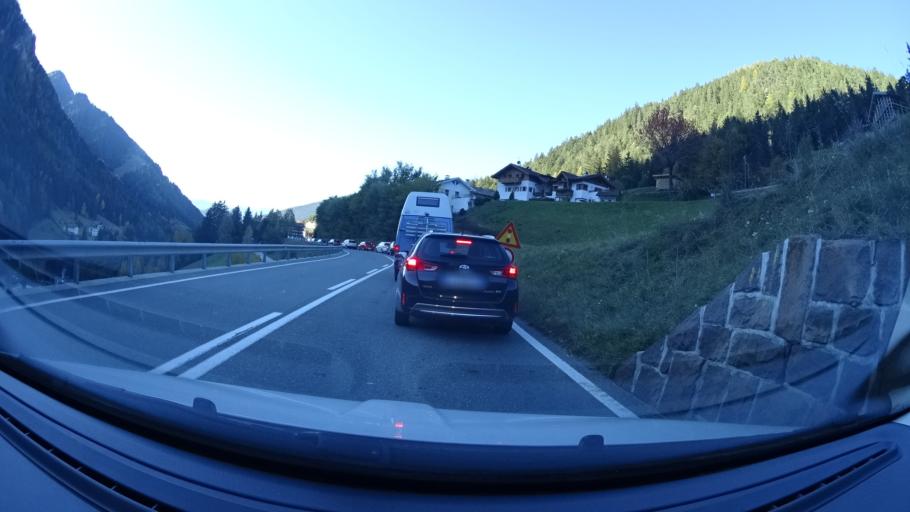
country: IT
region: Trentino-Alto Adige
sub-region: Bolzano
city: Santa Cristina Valgardena
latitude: 46.5625
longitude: 11.7021
